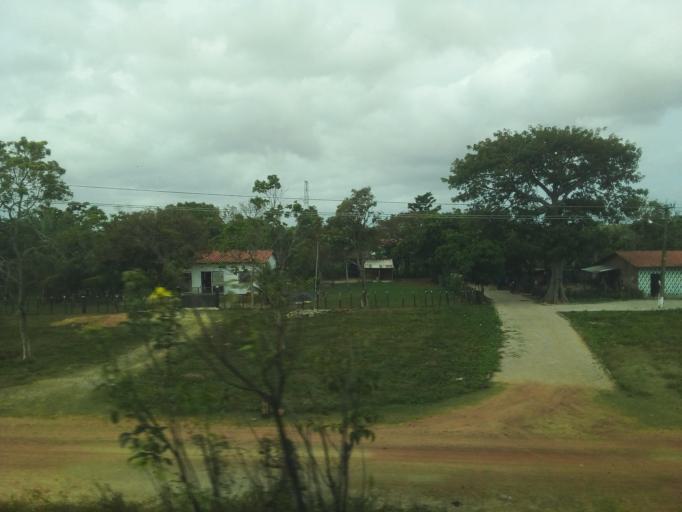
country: BR
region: Maranhao
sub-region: Icatu
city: Icatu
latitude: -2.9153
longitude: -44.3540
